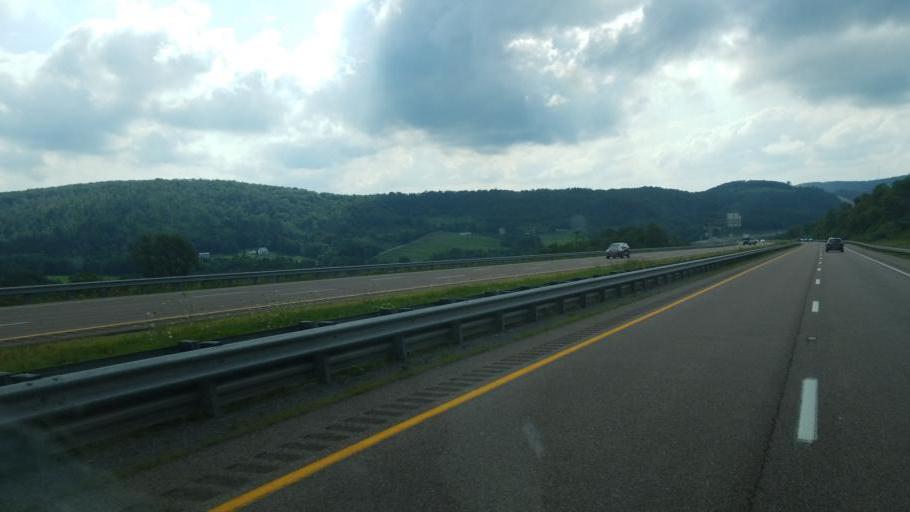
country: US
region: Pennsylvania
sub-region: Somerset County
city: Meyersdale
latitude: 39.6947
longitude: -79.2624
